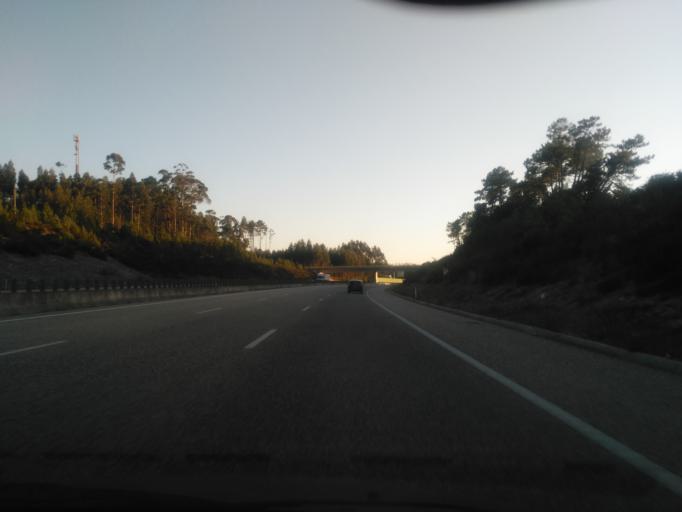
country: PT
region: Leiria
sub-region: Leiria
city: Monte Redondo
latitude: 39.9290
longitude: -8.7805
